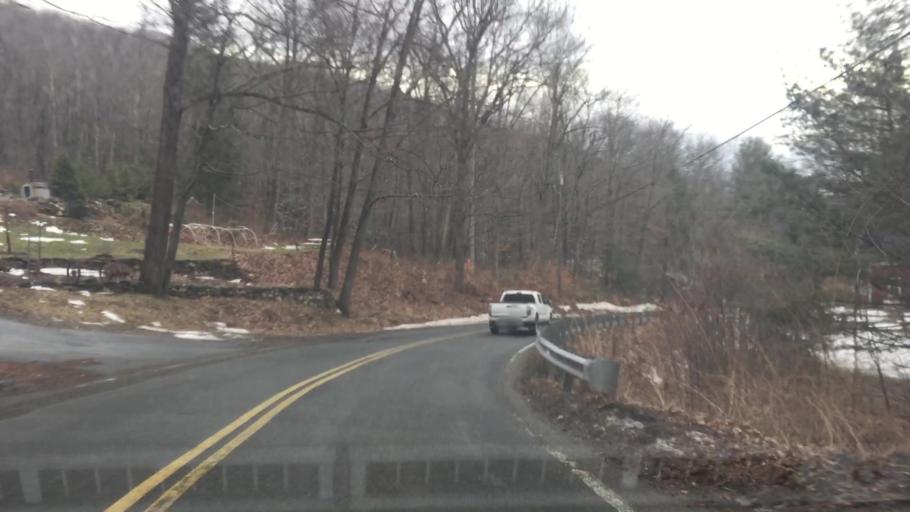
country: US
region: Massachusetts
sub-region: Hampshire County
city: Southampton
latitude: 42.2063
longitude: -72.8460
